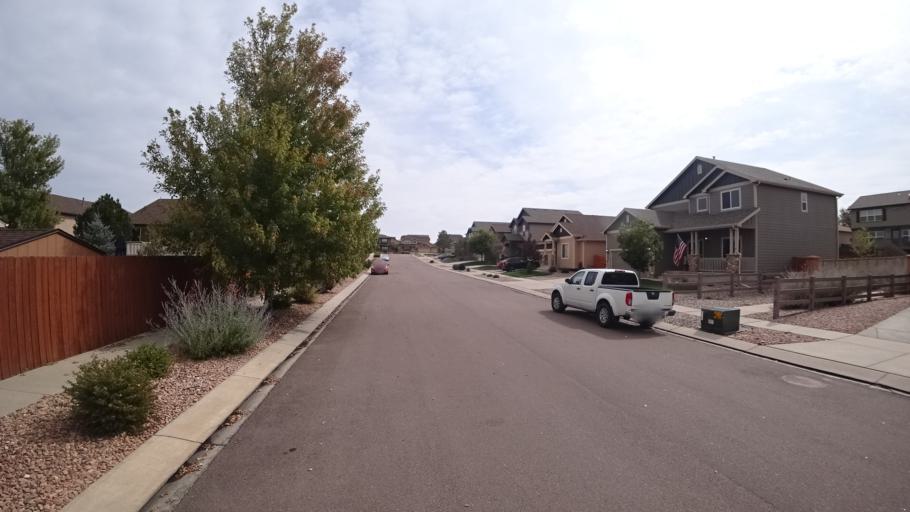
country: US
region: Colorado
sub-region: El Paso County
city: Cimarron Hills
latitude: 38.9217
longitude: -104.6912
